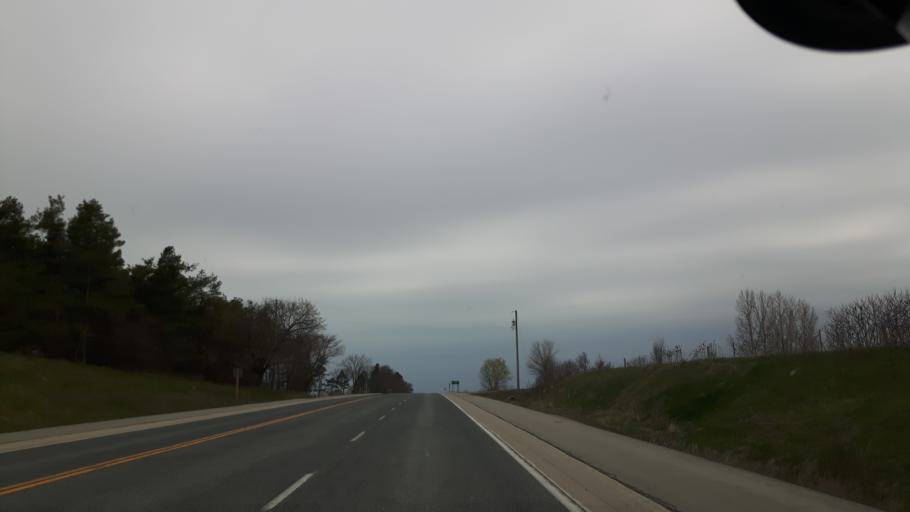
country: CA
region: Ontario
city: Goderich
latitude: 43.6499
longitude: -81.6069
